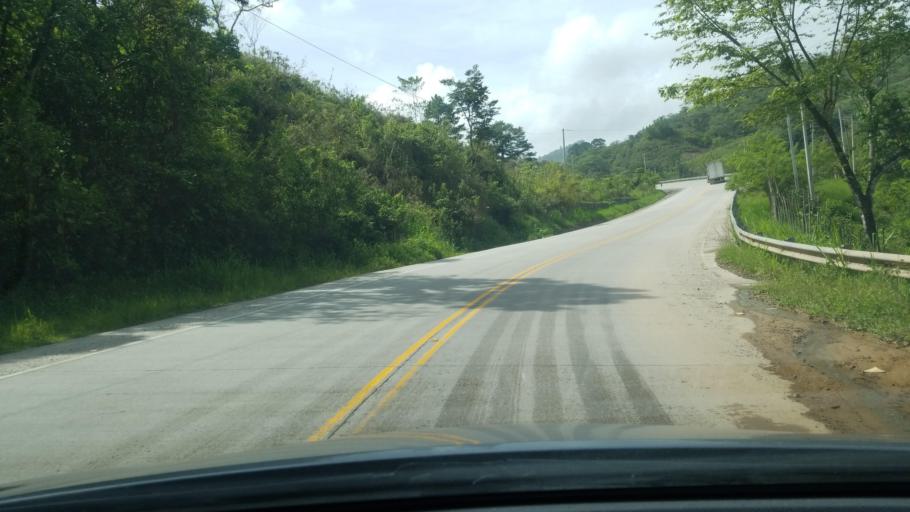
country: HN
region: Copan
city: San Jeronimo
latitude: 14.9302
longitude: -88.9388
